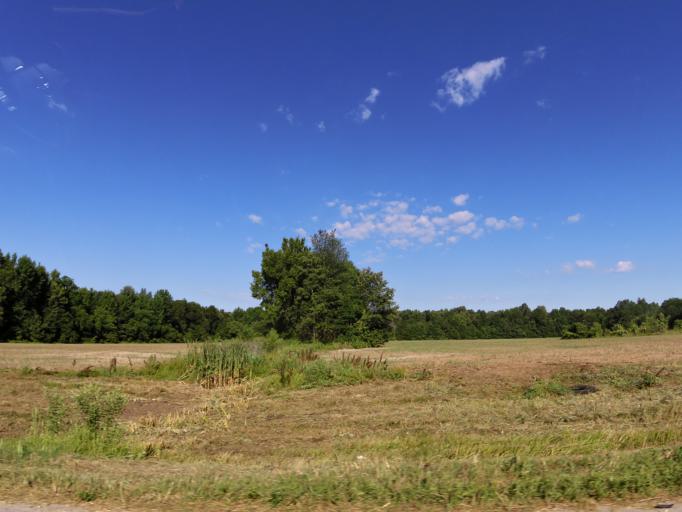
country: US
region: Arkansas
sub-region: Clay County
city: Corning
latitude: 36.5592
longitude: -90.5210
